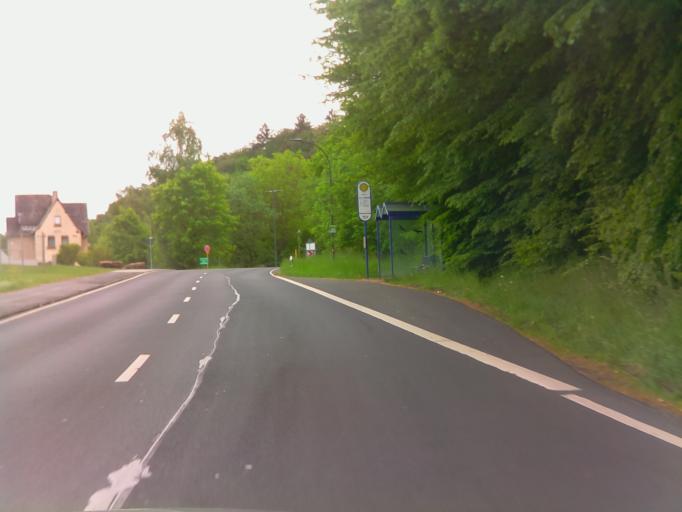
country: DE
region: Hesse
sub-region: Regierungsbezirk Giessen
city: Homberg
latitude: 50.7216
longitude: 9.0053
